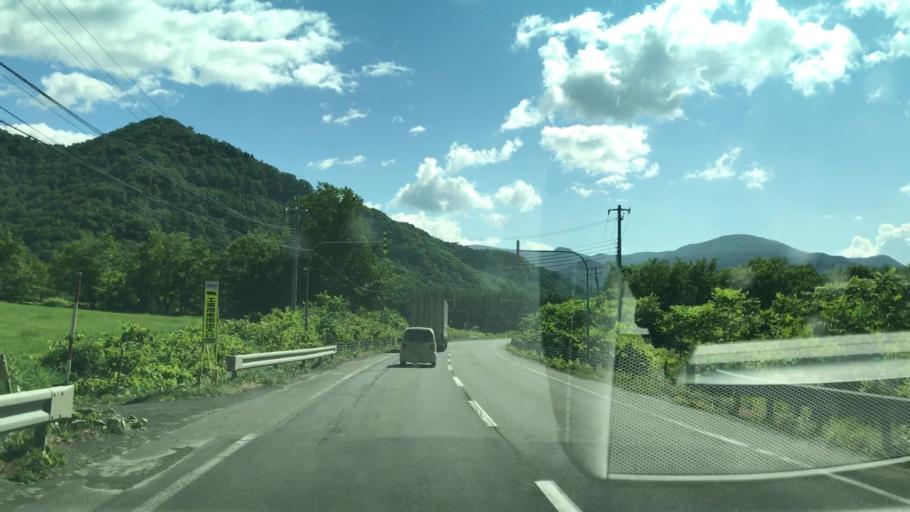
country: JP
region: Hokkaido
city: Shimo-furano
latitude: 42.9003
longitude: 142.5639
